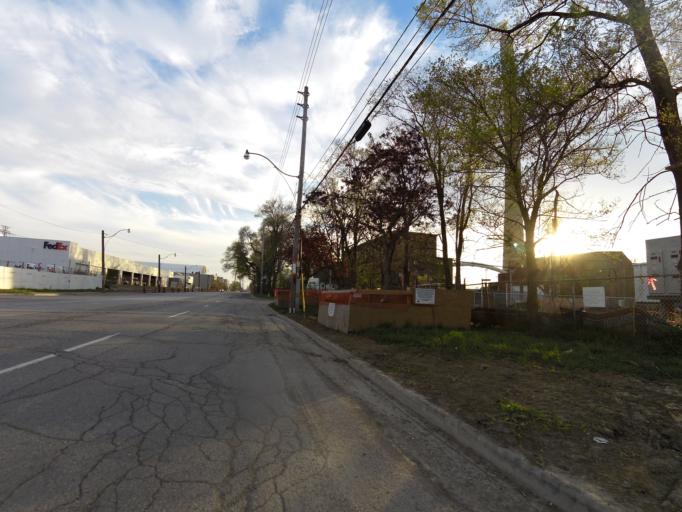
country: CA
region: Ontario
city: Toronto
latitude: 43.6519
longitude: -79.3373
